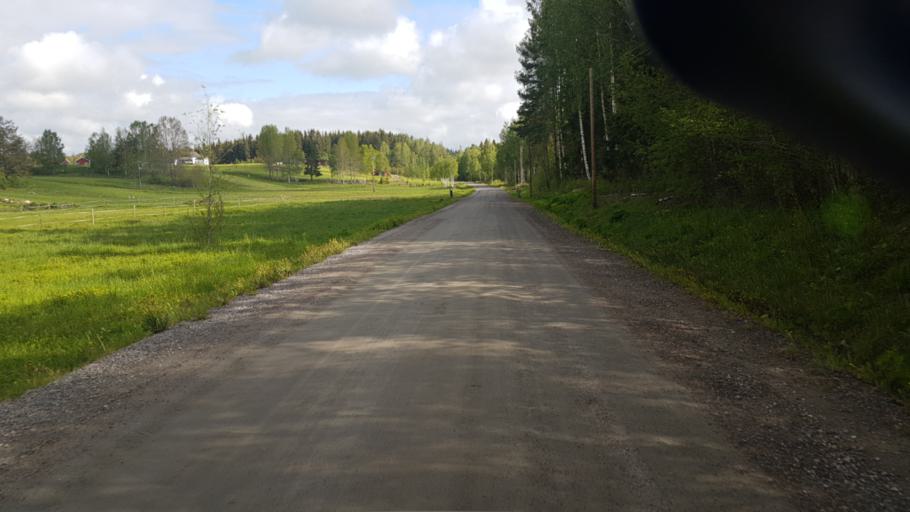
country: NO
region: Hedmark
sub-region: Eidskog
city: Skotterud
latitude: 59.8474
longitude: 11.9839
